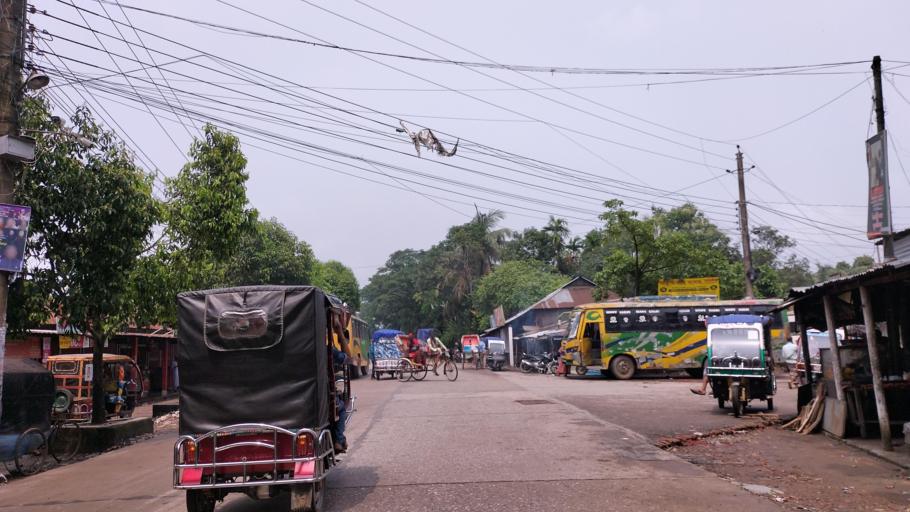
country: BD
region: Dhaka
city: Netrakona
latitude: 24.8942
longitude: 90.7406
